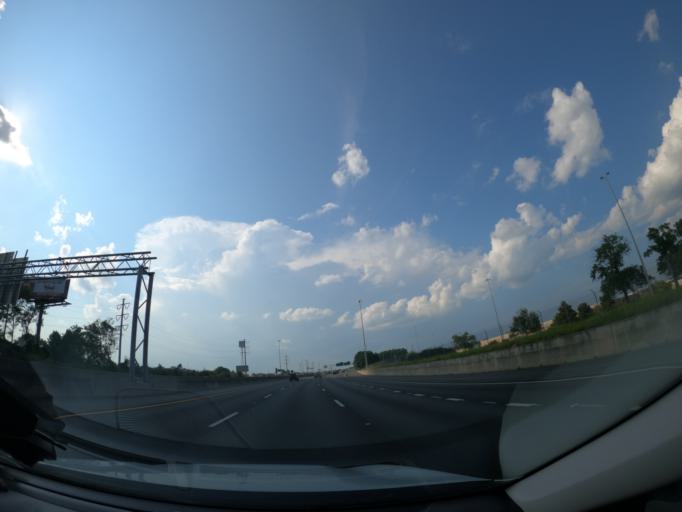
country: US
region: Georgia
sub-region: Columbia County
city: Martinez
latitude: 33.4617
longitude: -82.0814
